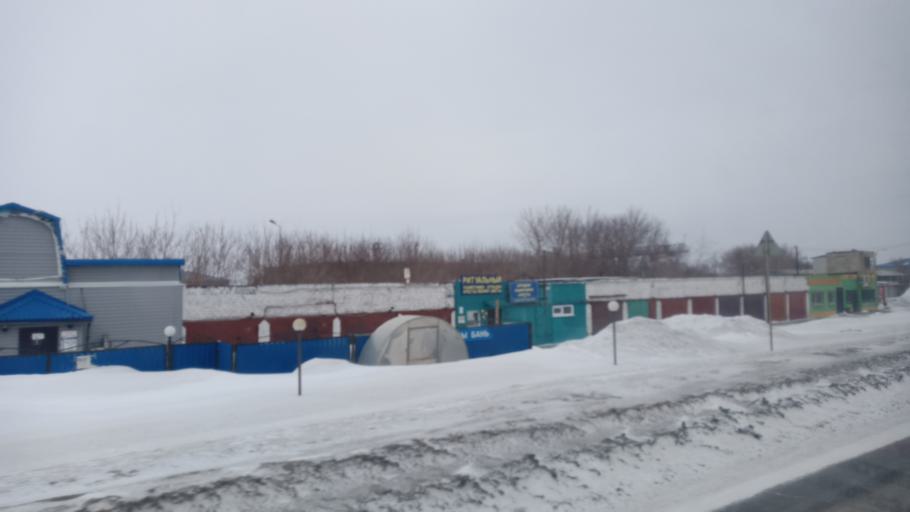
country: RU
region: Altai Krai
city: Novosilikatnyy
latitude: 53.3899
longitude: 83.6735
